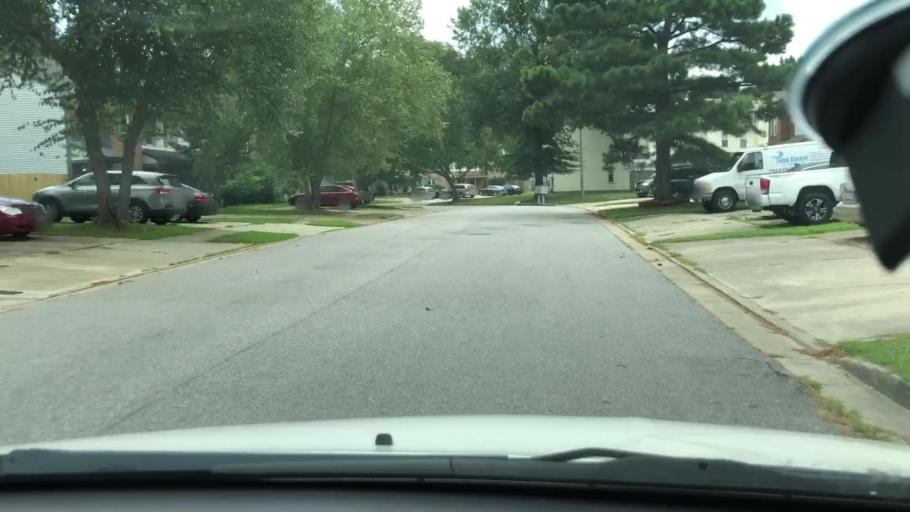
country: US
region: Virginia
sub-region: City of Virginia Beach
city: Virginia Beach
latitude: 36.8436
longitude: -76.1132
